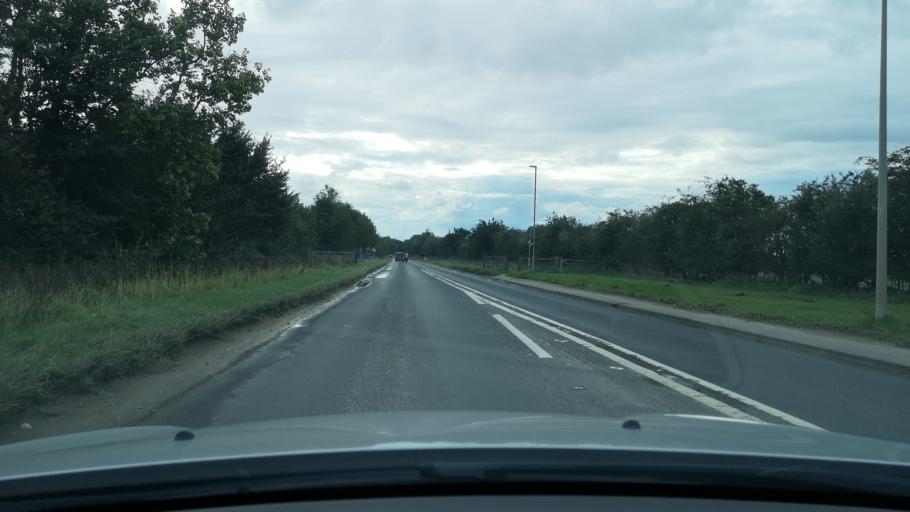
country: GB
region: England
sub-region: East Riding of Yorkshire
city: North Cave
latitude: 53.7746
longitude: -0.6661
